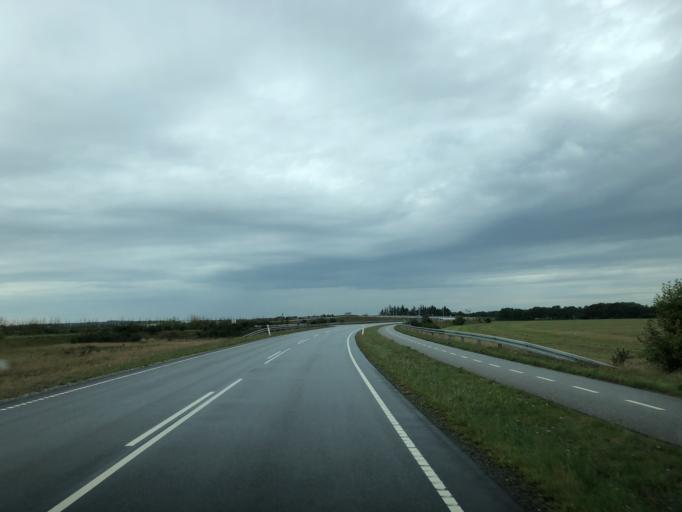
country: DK
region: Central Jutland
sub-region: Herning Kommune
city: Lind
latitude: 56.0125
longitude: 9.0328
